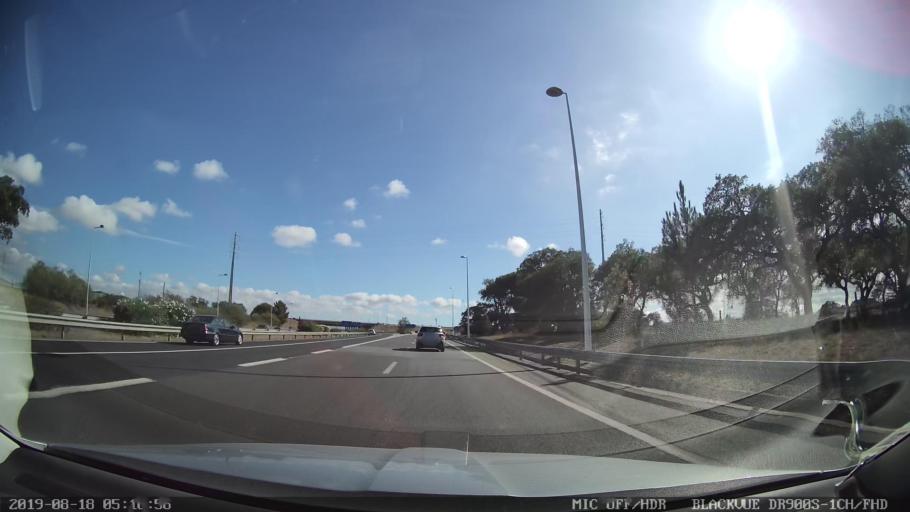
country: PT
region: Setubal
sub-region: Montijo
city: Montijo
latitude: 38.7207
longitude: -8.9410
